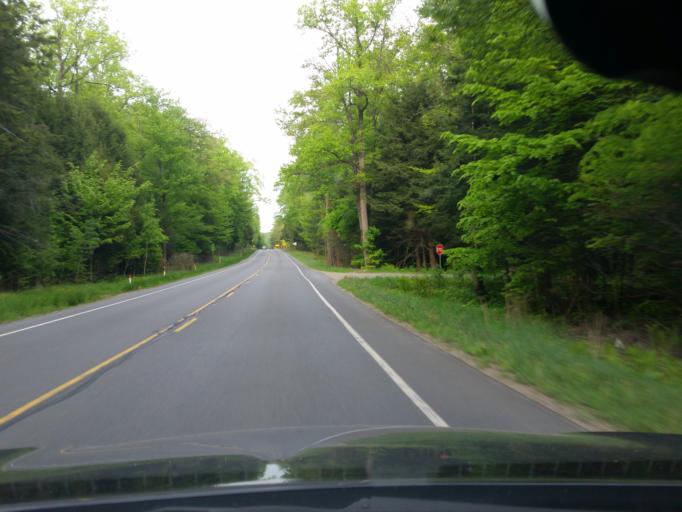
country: US
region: Pennsylvania
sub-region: McKean County
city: Kane
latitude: 41.5698
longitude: -78.8960
